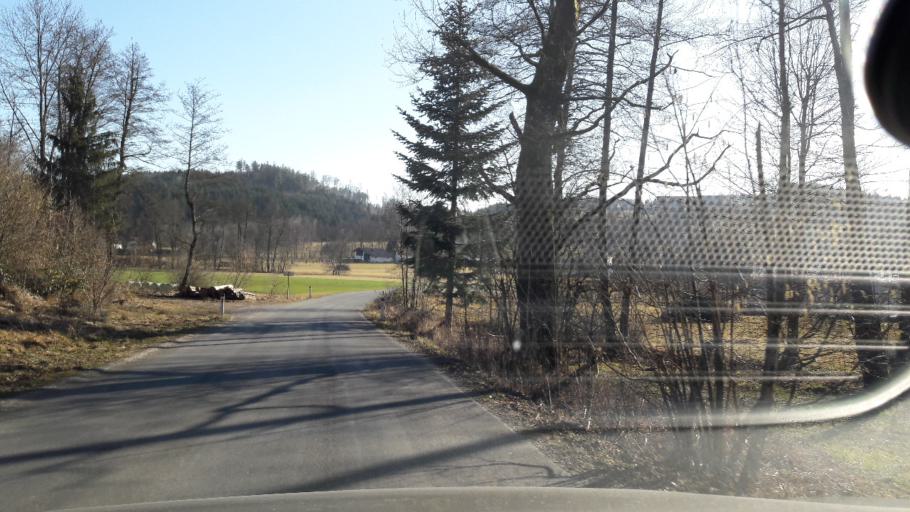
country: AT
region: Styria
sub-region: Politischer Bezirk Graz-Umgebung
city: Eisbach
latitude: 47.1083
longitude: 15.2739
